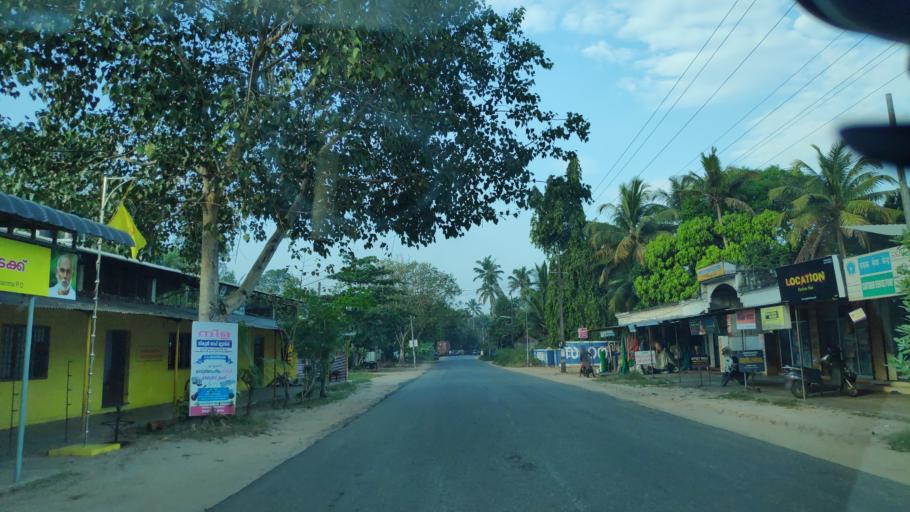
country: IN
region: Kerala
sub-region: Alappuzha
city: Shertallai
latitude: 9.6180
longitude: 76.3638
